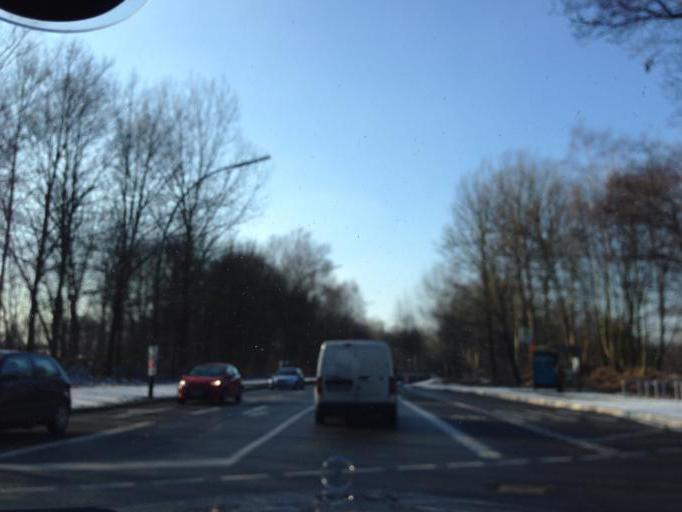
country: DE
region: Hamburg
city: Farmsen-Berne
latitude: 53.6060
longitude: 10.1066
